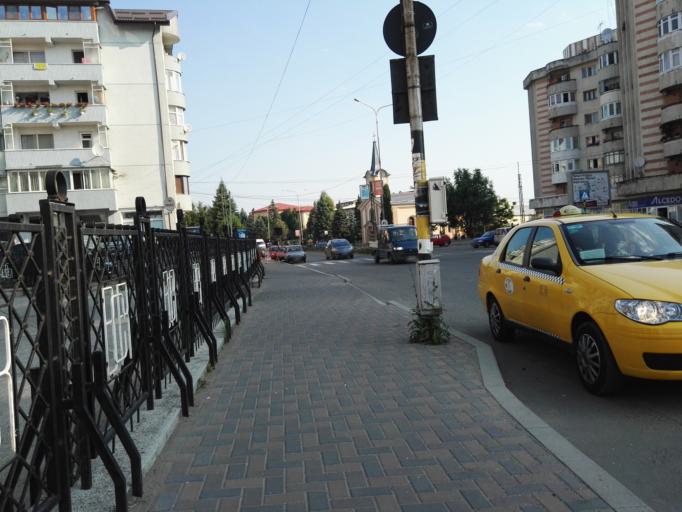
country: RO
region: Suceava
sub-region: Municipiul Falticeni
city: Falticeni
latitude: 47.4612
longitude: 26.3025
